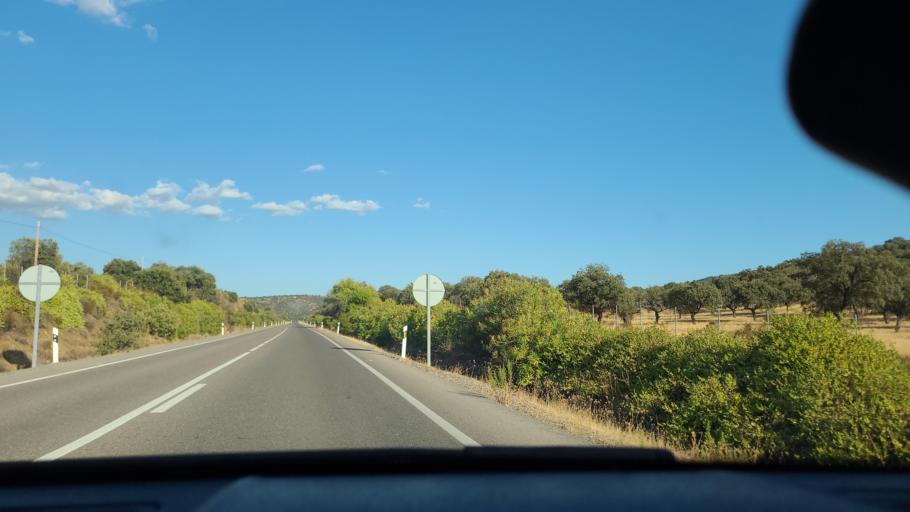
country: ES
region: Andalusia
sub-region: Province of Cordoba
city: Belmez
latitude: 38.2058
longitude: -5.1227
